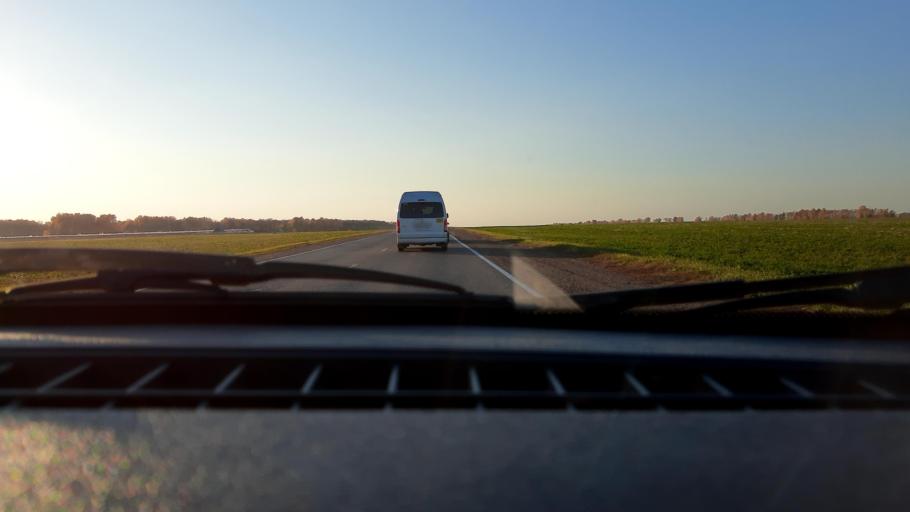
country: RU
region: Bashkortostan
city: Avdon
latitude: 54.8229
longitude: 55.6588
